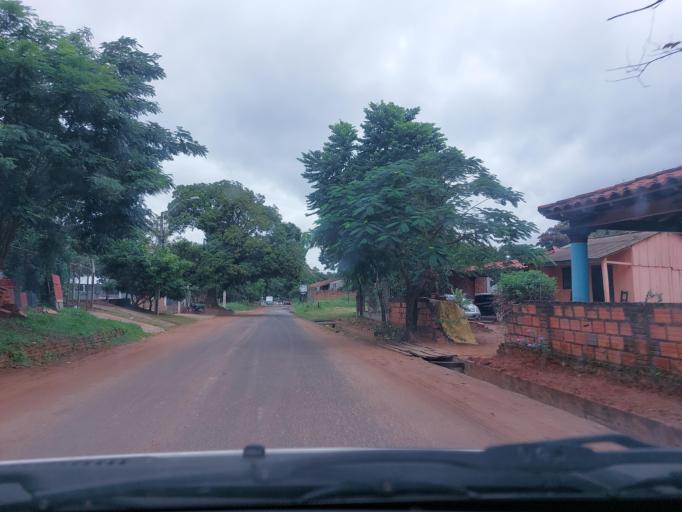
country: PY
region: San Pedro
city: Guayaybi
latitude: -24.6766
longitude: -56.4488
